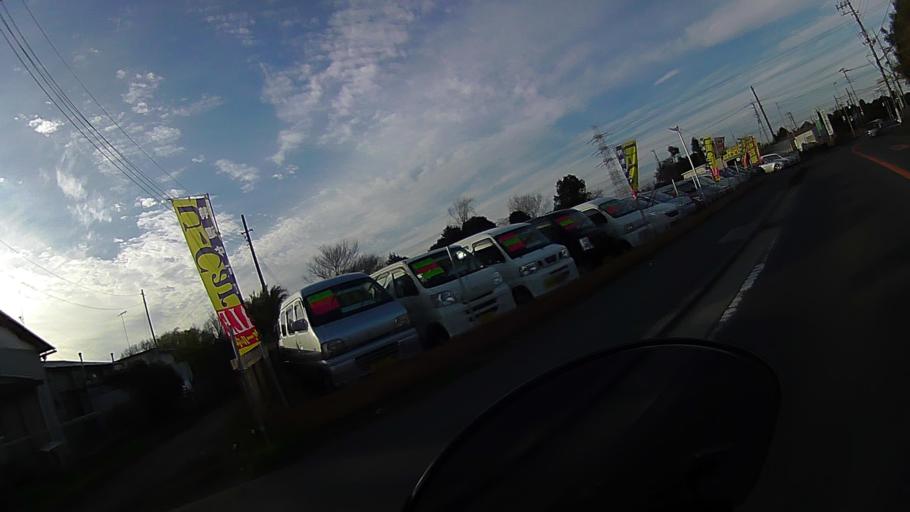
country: JP
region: Kanagawa
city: Atsugi
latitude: 35.4170
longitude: 139.4190
